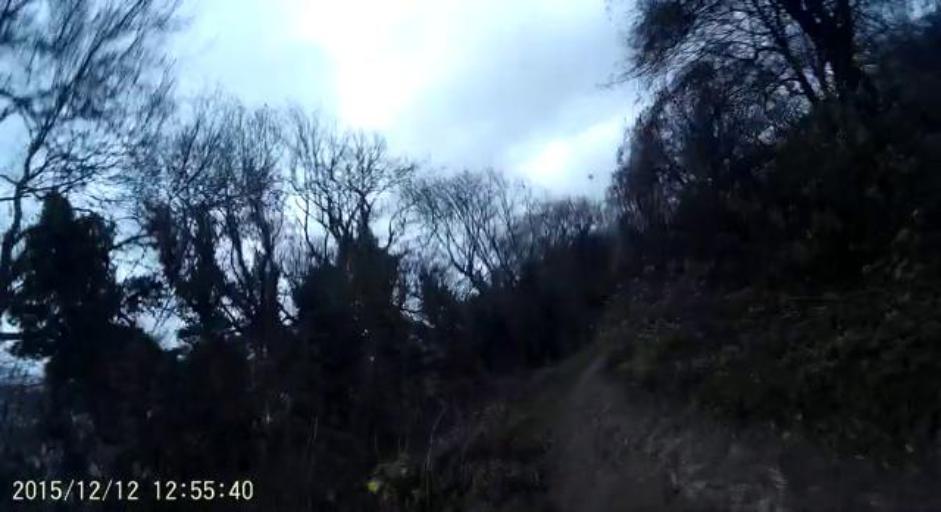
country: GB
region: England
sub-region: Hampshire
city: Petersfield
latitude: 50.9731
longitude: -0.9586
